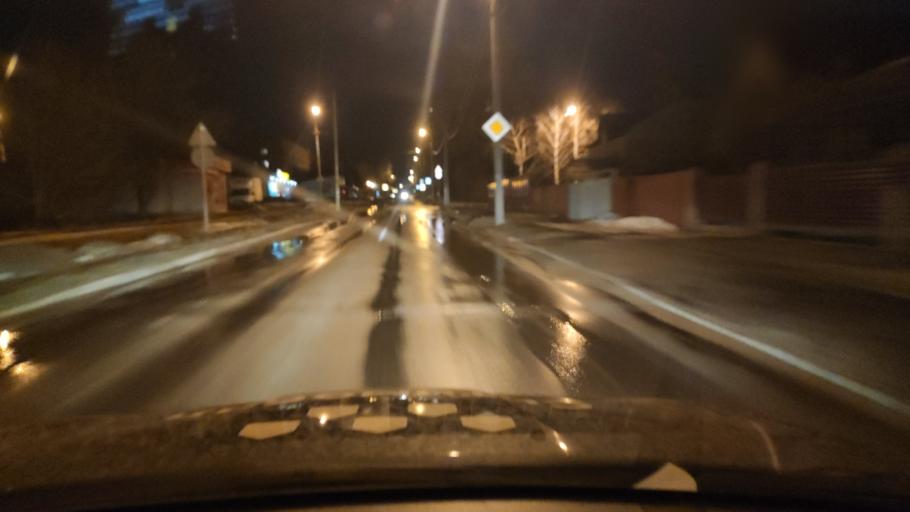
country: RU
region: Samara
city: Povolzhskiy
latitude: 53.5878
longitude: 49.7641
